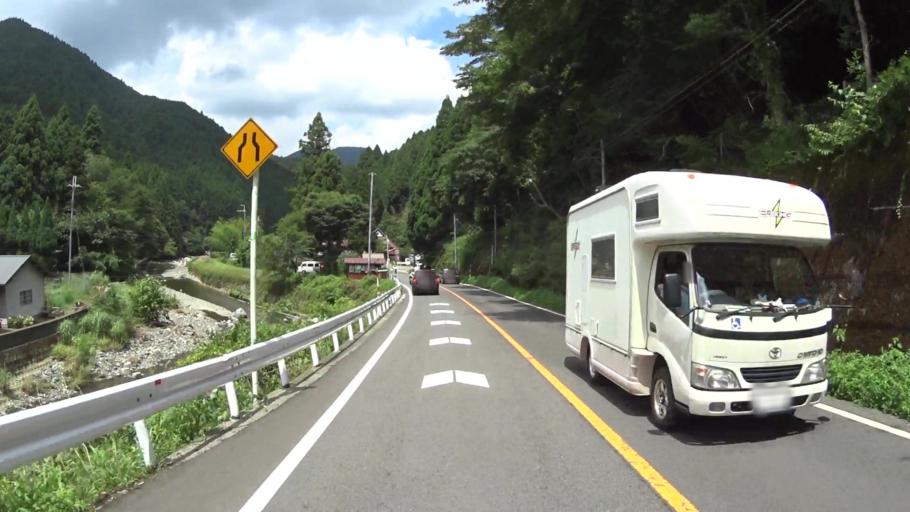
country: JP
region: Shiga Prefecture
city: Kitahama
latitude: 35.1973
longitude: 135.8613
